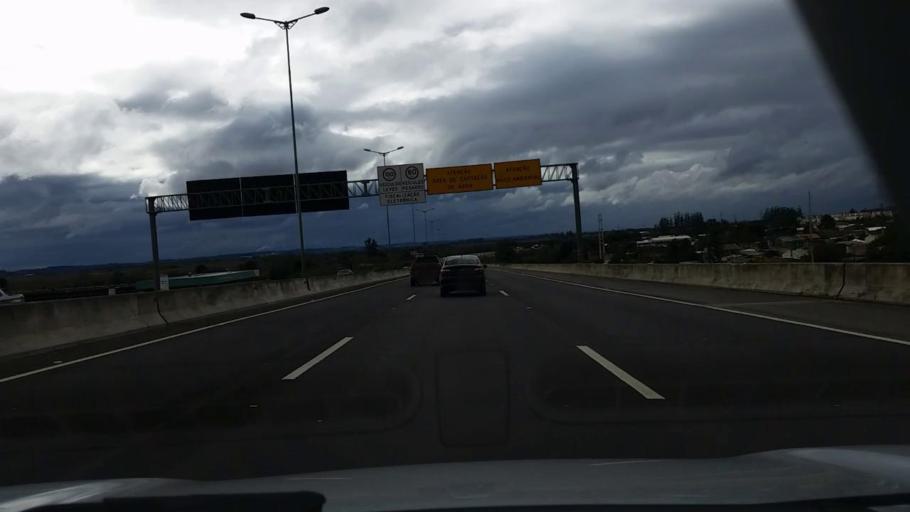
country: BR
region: Rio Grande do Sul
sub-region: Canoas
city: Canoas
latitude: -29.9681
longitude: -51.2012
